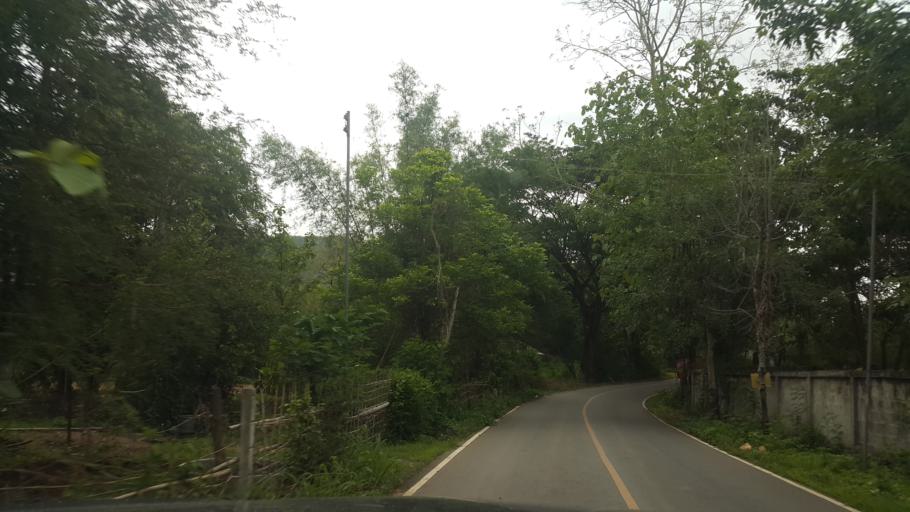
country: TH
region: Chiang Mai
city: Mae On
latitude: 18.7397
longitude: 99.2187
